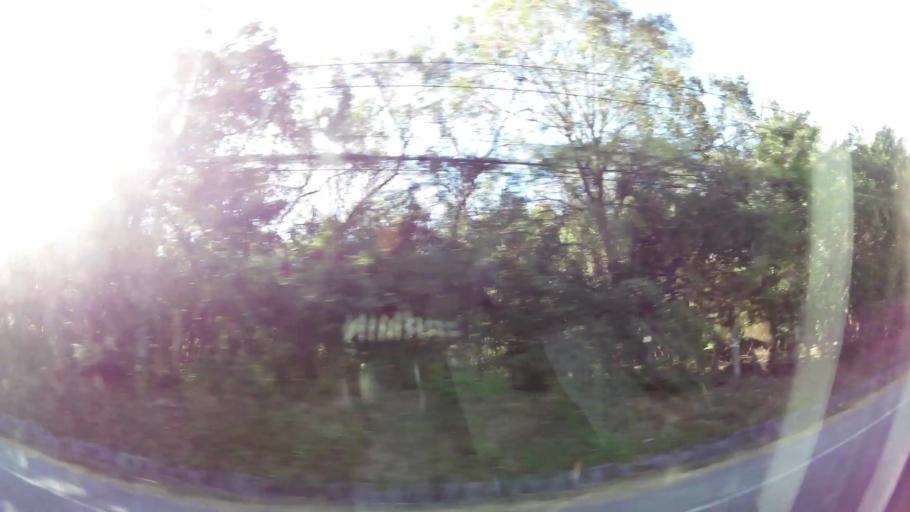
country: SV
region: Santa Ana
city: Santa Ana
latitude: 14.0089
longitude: -89.5458
